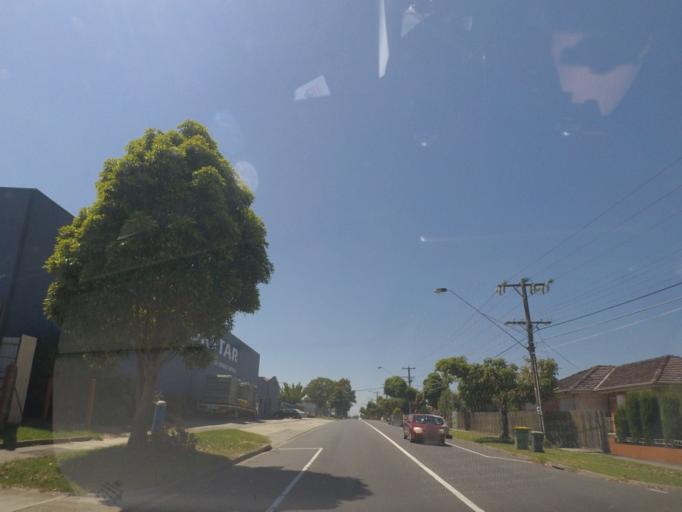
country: AU
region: Victoria
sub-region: Darebin
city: Reservoir
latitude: -37.7113
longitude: 144.9896
